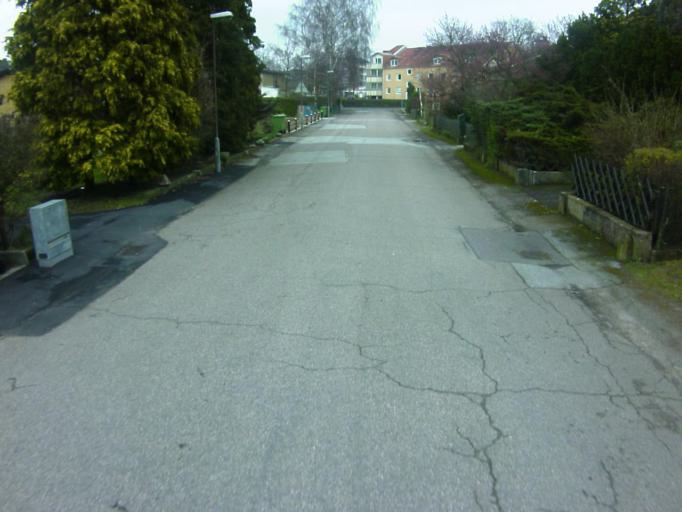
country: SE
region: Skane
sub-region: Kavlinge Kommun
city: Kaevlinge
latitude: 55.7724
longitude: 13.0878
